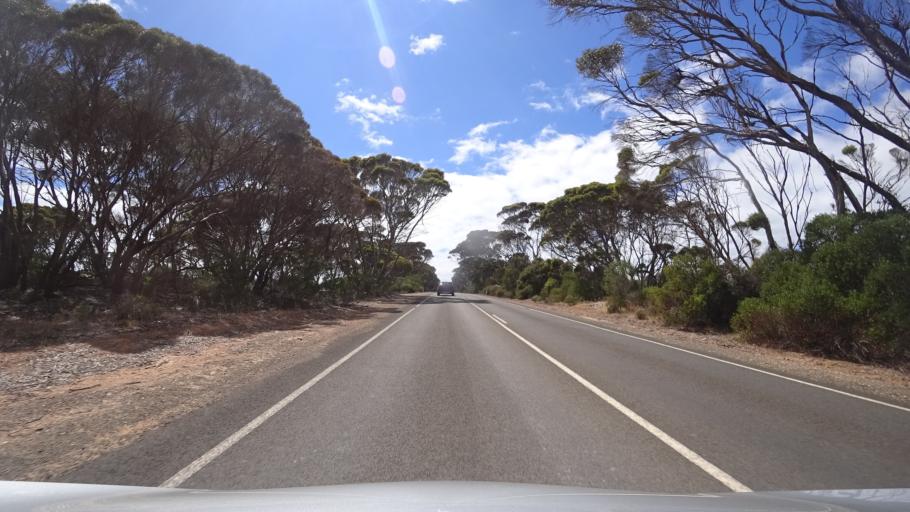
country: AU
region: South Australia
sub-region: Kangaroo Island
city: Kingscote
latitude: -35.6598
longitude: 137.5910
